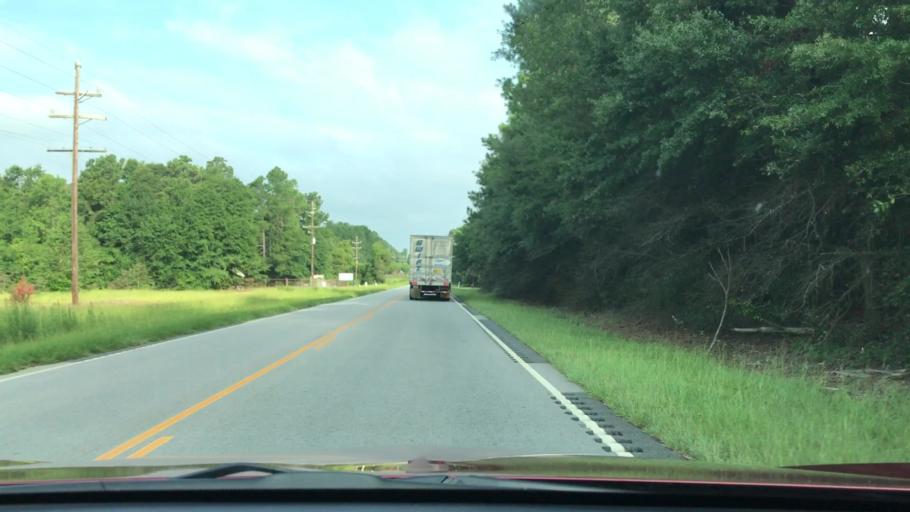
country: US
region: South Carolina
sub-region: Barnwell County
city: Williston
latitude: 33.6452
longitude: -81.3467
